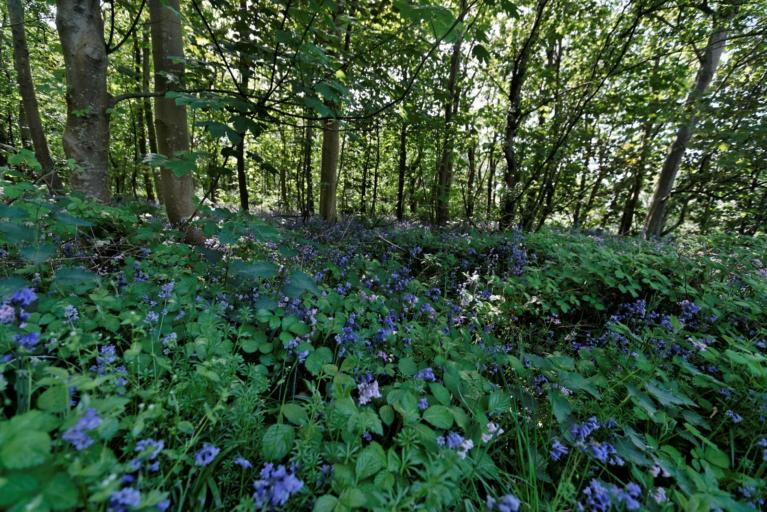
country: NL
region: North Holland
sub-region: Gemeente Texel
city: Den Burg
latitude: 53.0726
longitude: 4.7480
